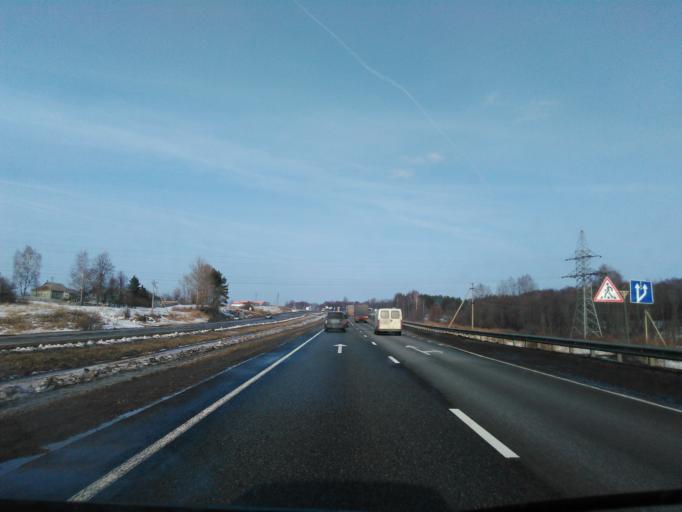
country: RU
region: Smolensk
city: Vyaz'ma
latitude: 55.2071
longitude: 34.1522
